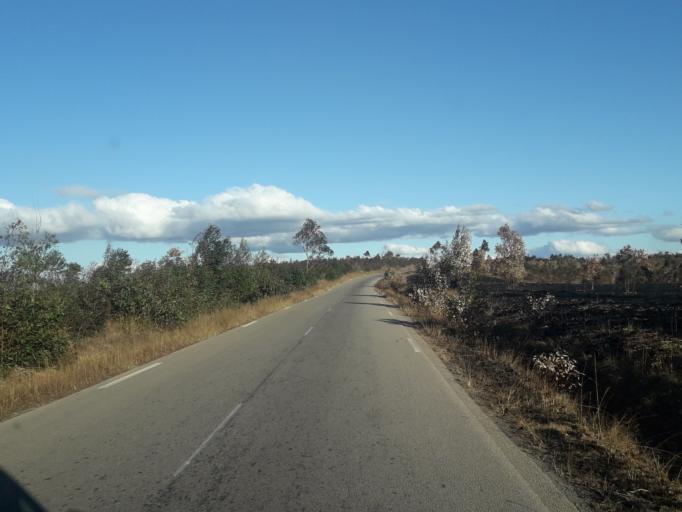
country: MG
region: Analamanga
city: Ankazobe
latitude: -18.1282
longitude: 47.2181
